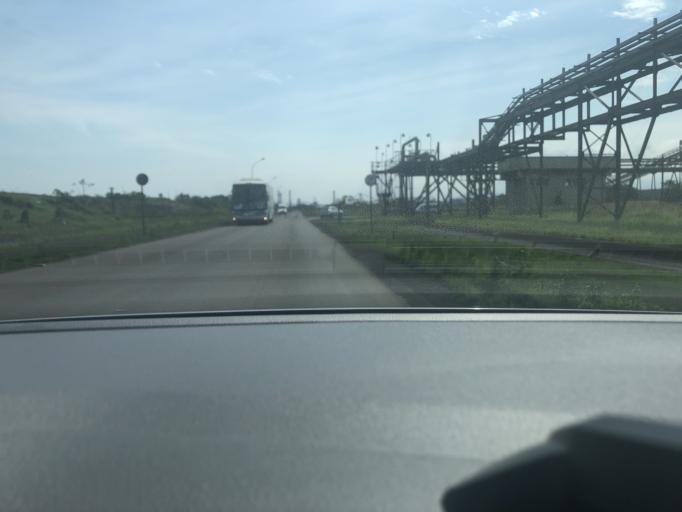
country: BR
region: Rio de Janeiro
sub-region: Itaguai
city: Itaguai
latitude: -22.9153
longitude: -43.7406
